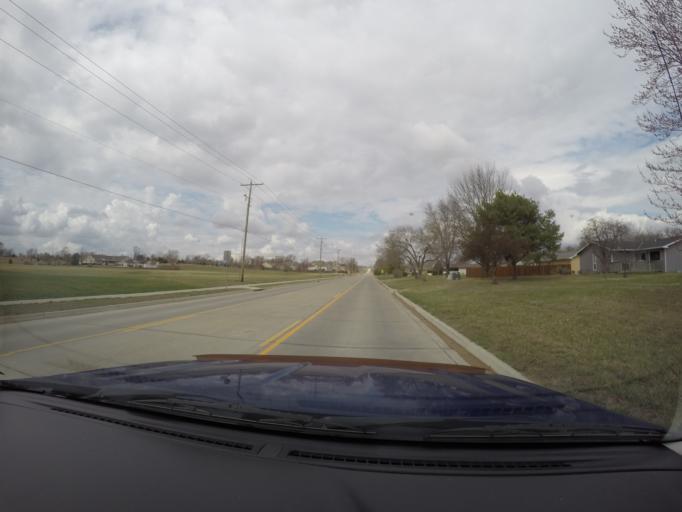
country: US
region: Kansas
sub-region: Riley County
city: Manhattan
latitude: 39.2074
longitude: -96.5106
